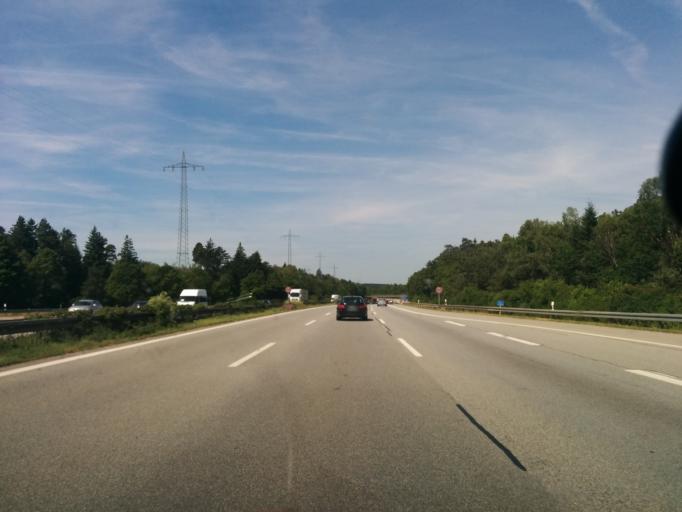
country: DE
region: Bavaria
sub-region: Upper Bavaria
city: Germering
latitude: 48.1172
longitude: 11.3836
